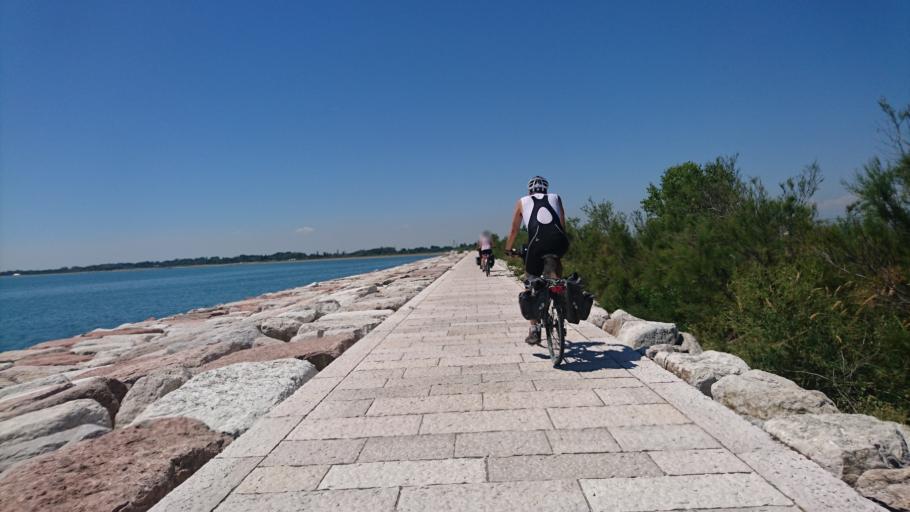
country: IT
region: Veneto
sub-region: Provincia di Venezia
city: Lido
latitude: 45.4273
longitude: 12.4116
